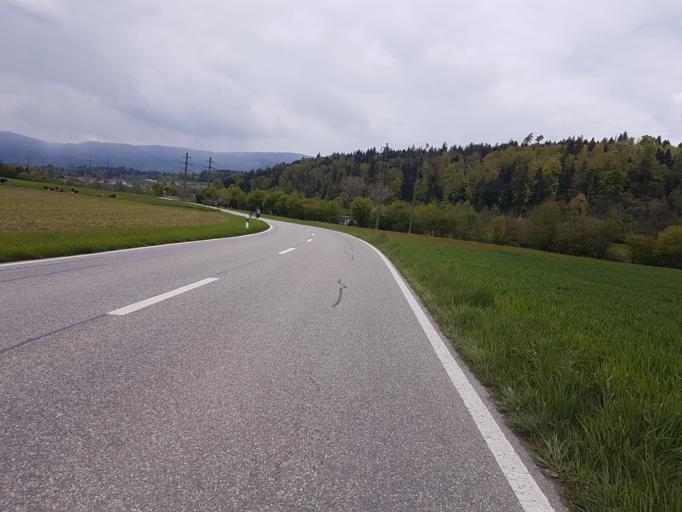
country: CH
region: Bern
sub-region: Oberaargau
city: Niederbipp
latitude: 47.2290
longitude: 7.7086
